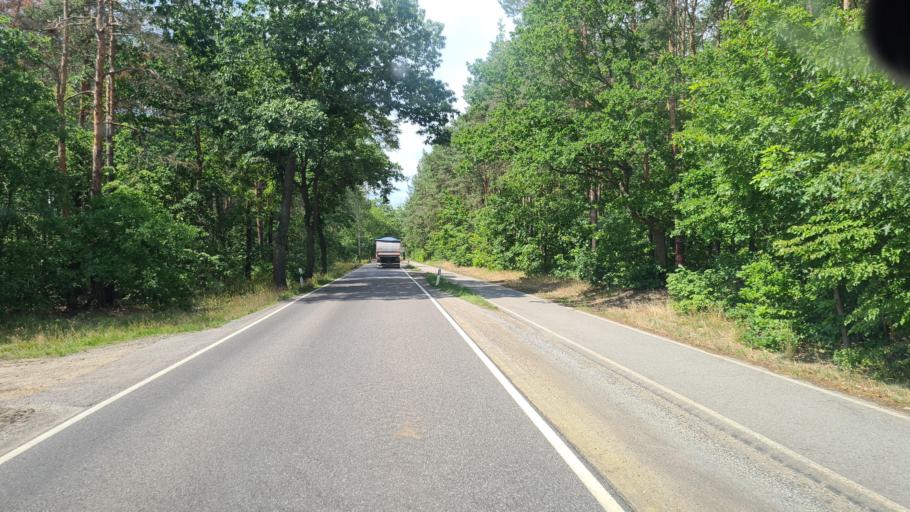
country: DE
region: Brandenburg
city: Welzow
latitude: 51.4918
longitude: 14.1421
